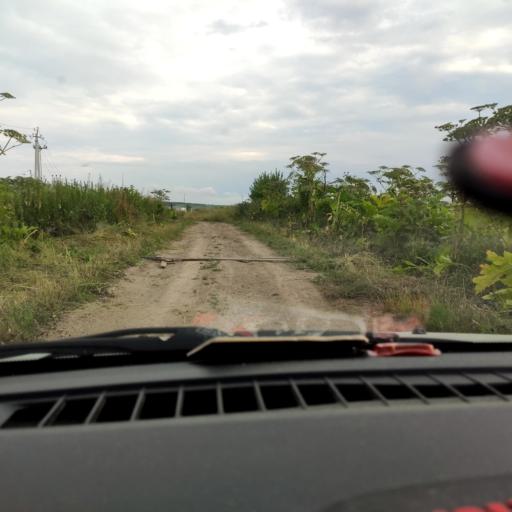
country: RU
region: Perm
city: Kultayevo
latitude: 57.8551
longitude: 55.9685
